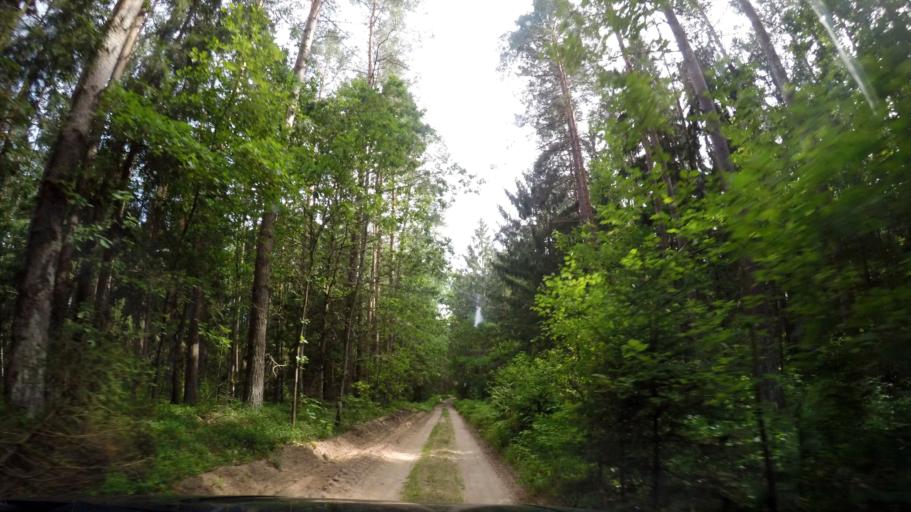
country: BY
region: Grodnenskaya
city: Skidal'
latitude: 53.8300
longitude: 24.1782
